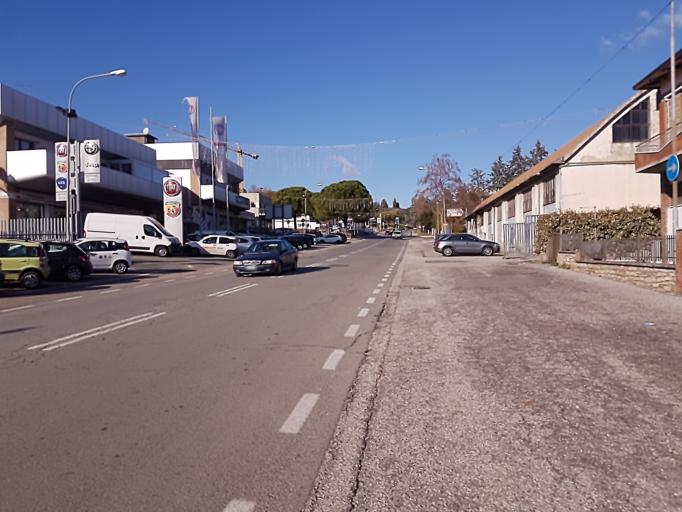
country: IT
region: Umbria
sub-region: Provincia di Perugia
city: Perugia
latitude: 43.0914
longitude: 12.3677
